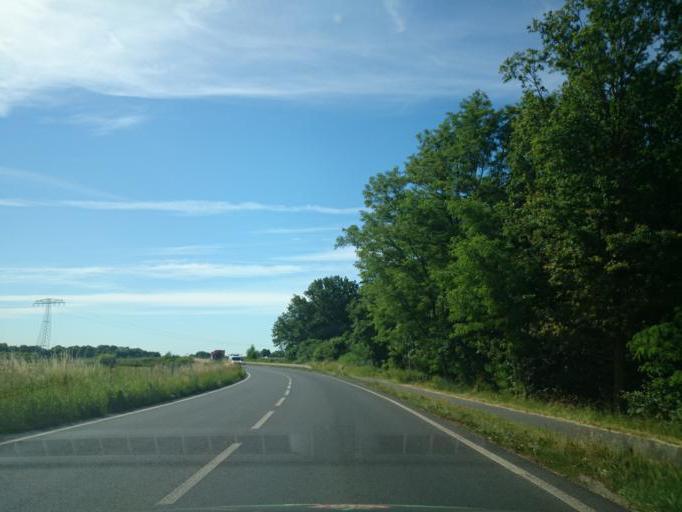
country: DE
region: Brandenburg
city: Teltow
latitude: 52.3635
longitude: 13.2669
